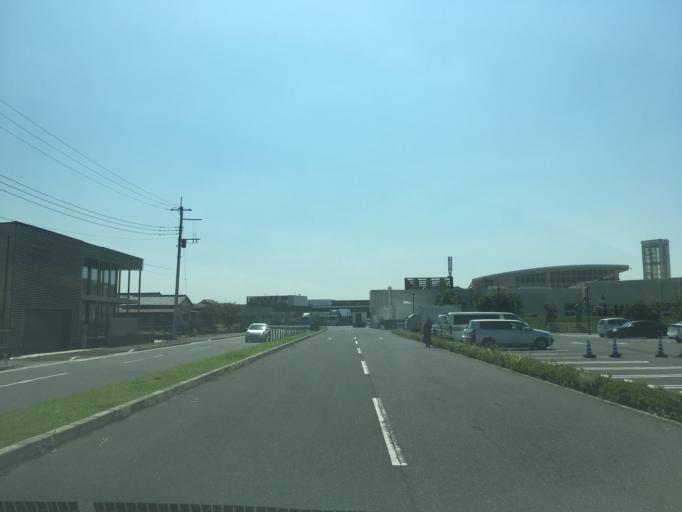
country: JP
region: Chiba
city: Kisarazu
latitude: 35.4368
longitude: 139.9356
